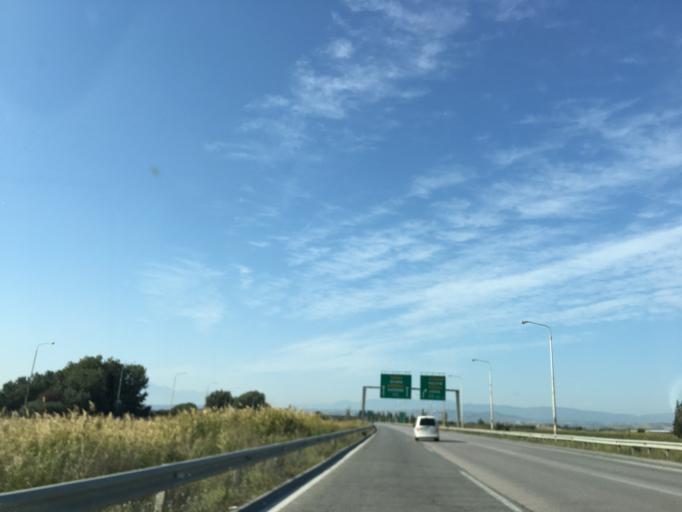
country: GR
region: Central Macedonia
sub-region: Nomos Imathias
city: Kleidi
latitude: 40.5630
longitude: 22.6065
